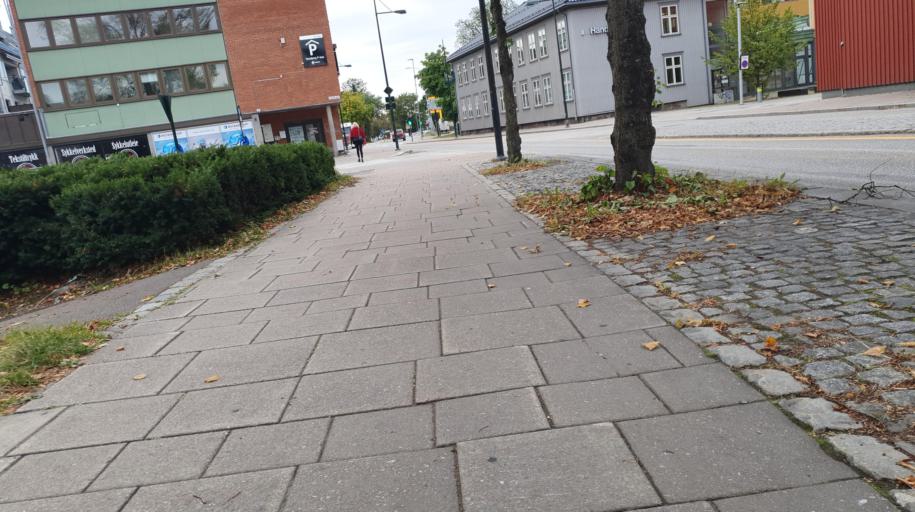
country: NO
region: Vestfold
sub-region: Tonsberg
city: Tonsberg
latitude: 59.2658
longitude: 10.4078
